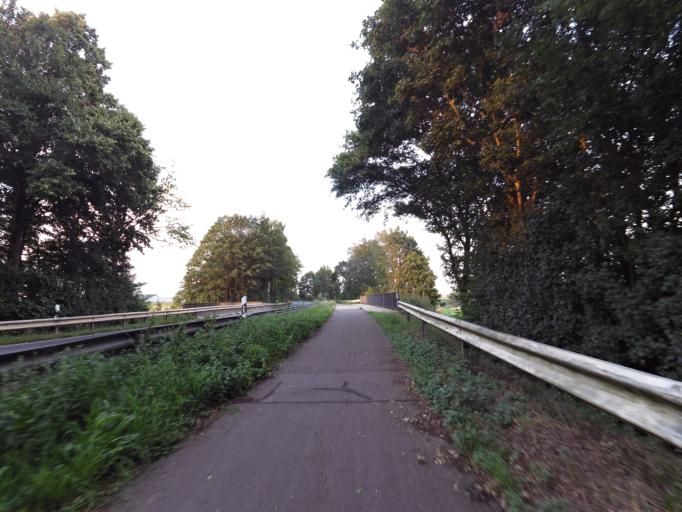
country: DE
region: North Rhine-Westphalia
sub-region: Regierungsbezirk Dusseldorf
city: Kleve
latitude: 51.8178
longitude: 6.1727
